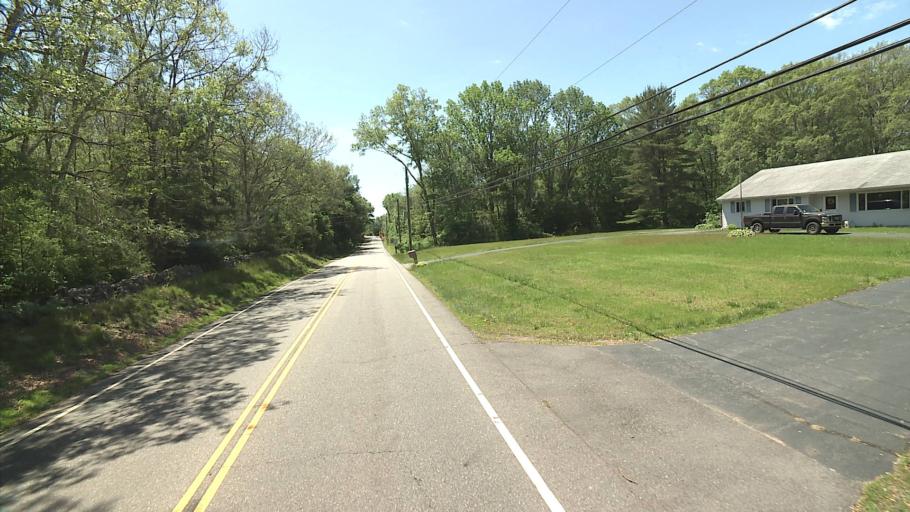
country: US
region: Rhode Island
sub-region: Washington County
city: Hopkinton
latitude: 41.4581
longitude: -71.8360
